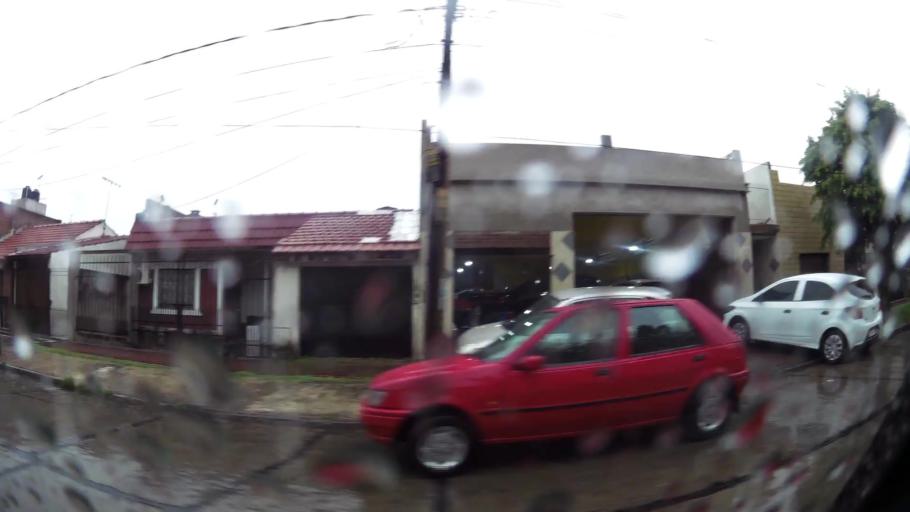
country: AR
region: Buenos Aires
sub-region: Partido de Lanus
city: Lanus
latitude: -34.7132
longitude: -58.4165
